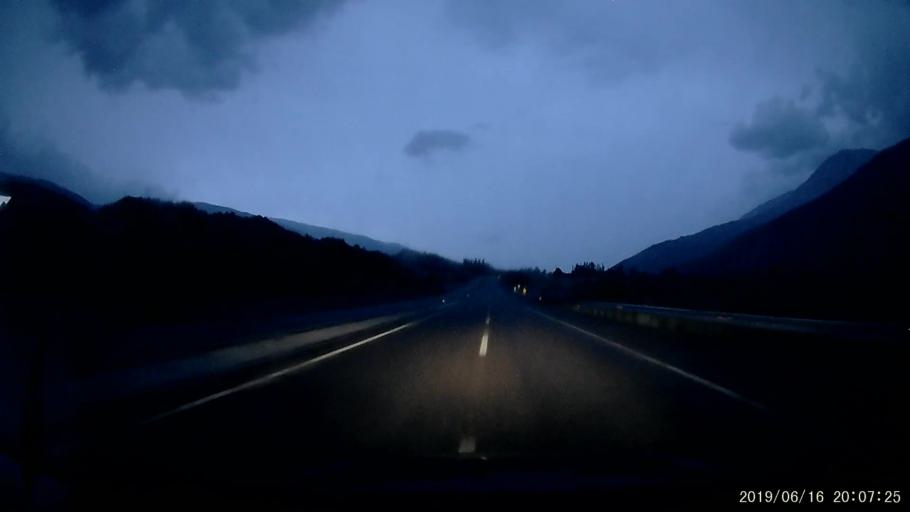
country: TR
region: Sivas
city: Dogansar
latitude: 40.3184
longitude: 37.6244
